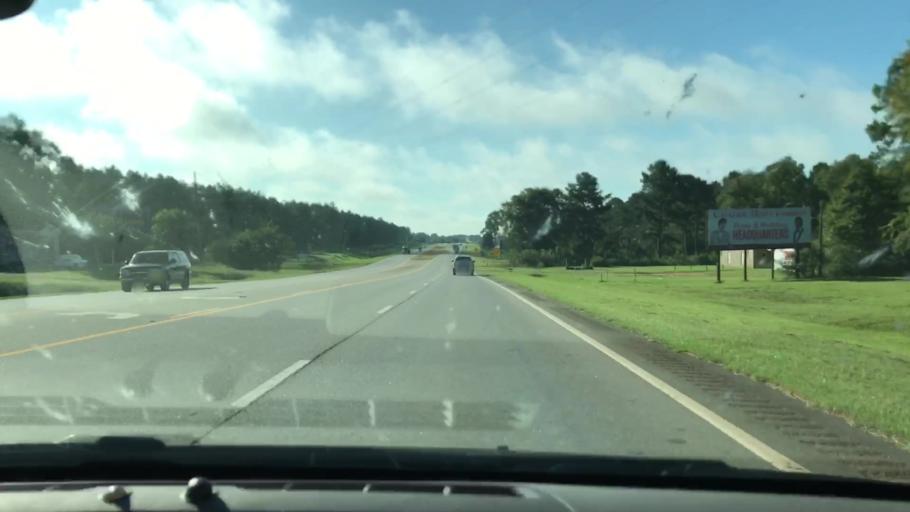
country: US
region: Georgia
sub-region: Terrell County
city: Dawson
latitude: 31.7522
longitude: -84.4231
